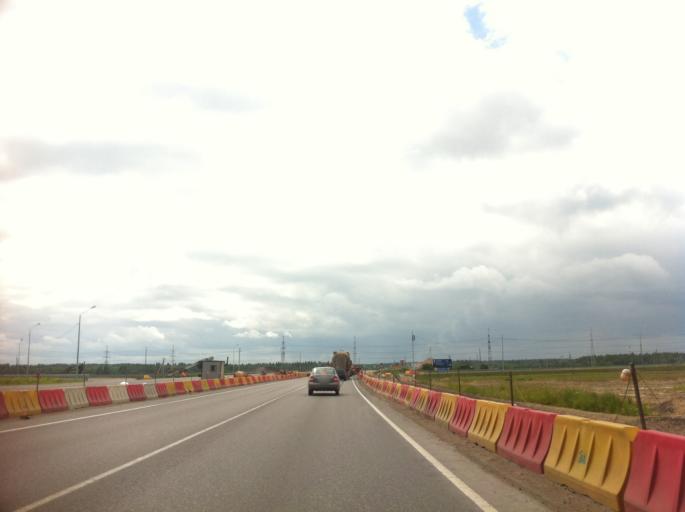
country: RU
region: Leningrad
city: Gatchina
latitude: 59.5344
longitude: 30.1537
